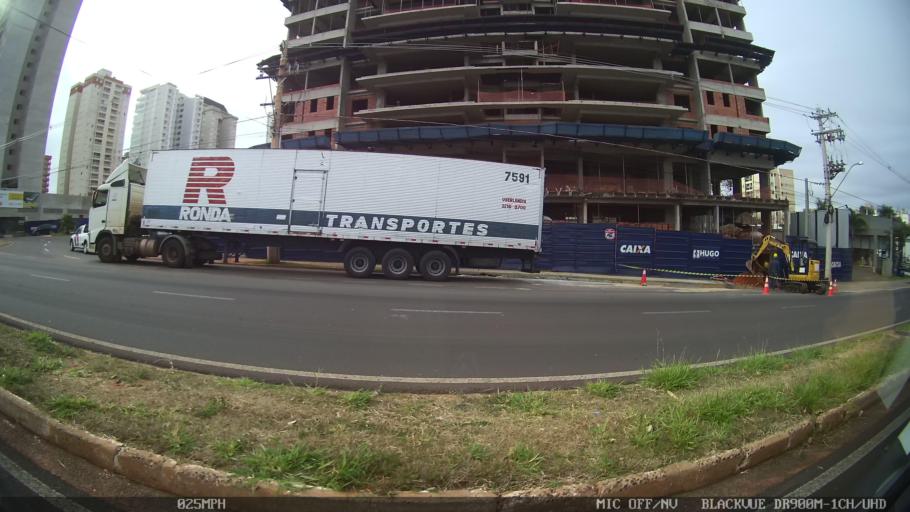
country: BR
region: Sao Paulo
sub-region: Sao Jose Do Rio Preto
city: Sao Jose do Rio Preto
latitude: -20.8289
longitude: -49.3853
